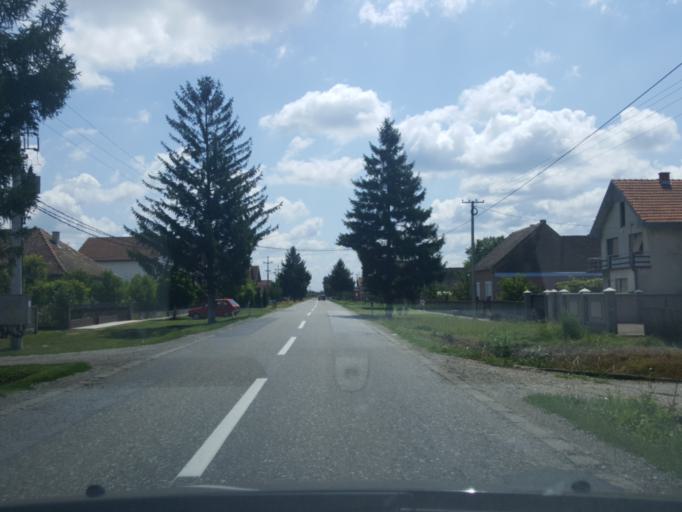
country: RS
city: Glusci
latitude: 44.8852
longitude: 19.5524
